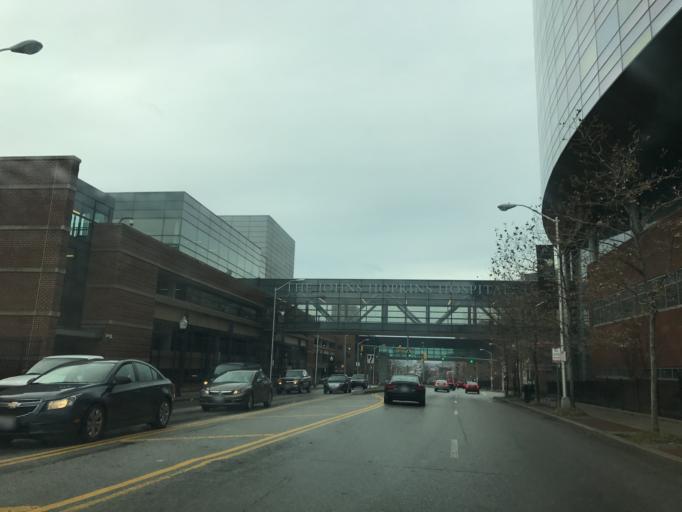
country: US
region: Maryland
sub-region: City of Baltimore
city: Baltimore
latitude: 39.2953
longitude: -76.5907
